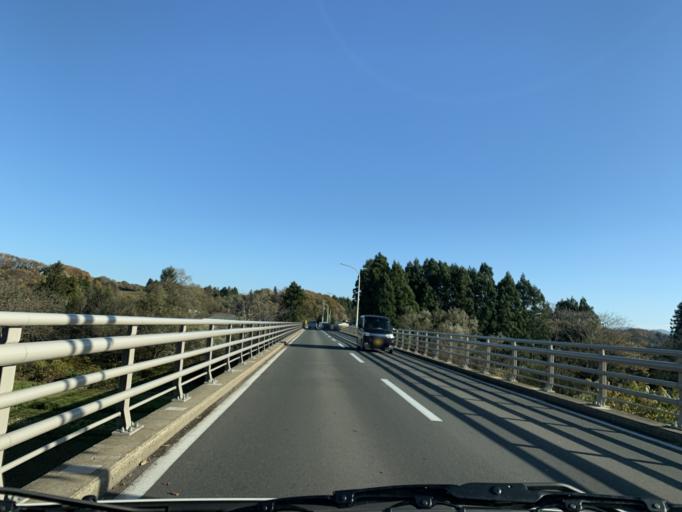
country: JP
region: Iwate
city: Kitakami
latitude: 39.2519
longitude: 141.1169
